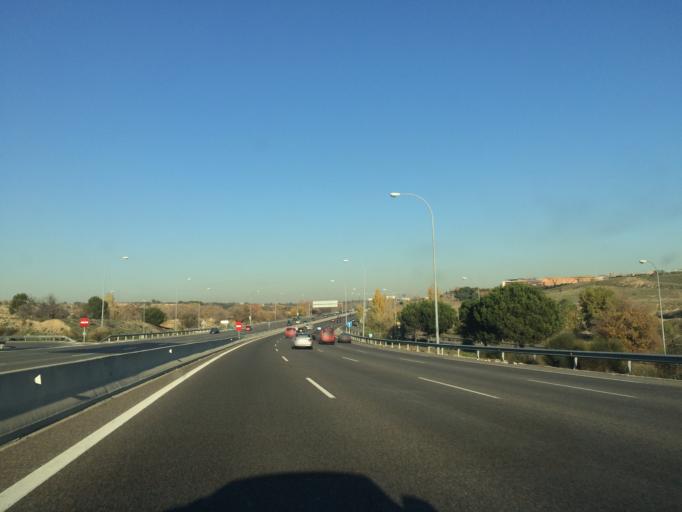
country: ES
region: Madrid
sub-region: Provincia de Madrid
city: Fuencarral-El Pardo
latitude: 40.5003
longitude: -3.7219
